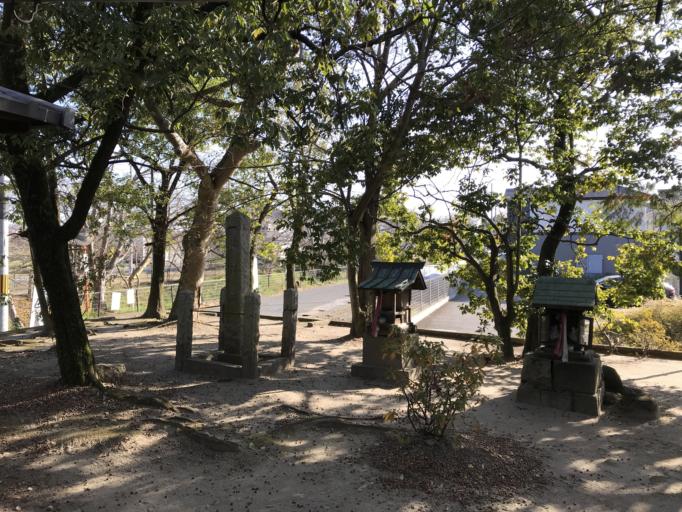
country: JP
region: Kyoto
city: Tanabe
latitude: 34.8189
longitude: 135.7761
